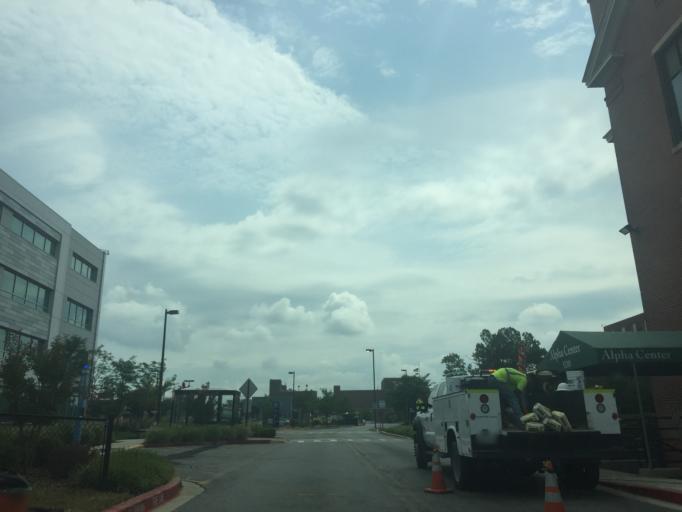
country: US
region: Maryland
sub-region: Baltimore County
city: Rosedale
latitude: 39.2904
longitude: -76.5519
